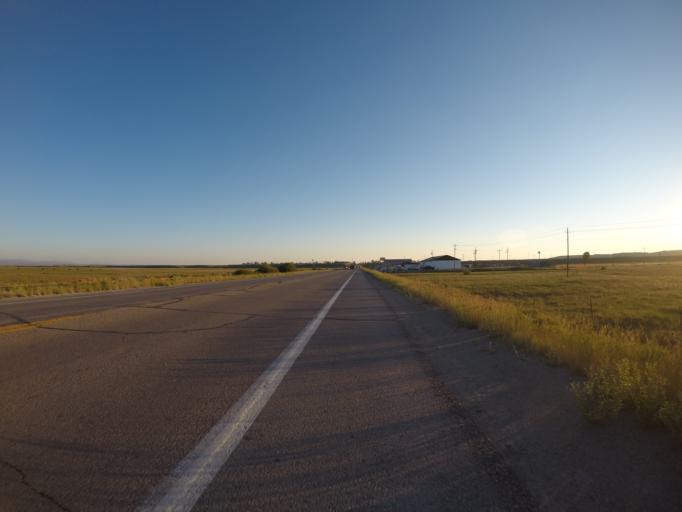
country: US
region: Wyoming
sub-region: Sublette County
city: Marbleton
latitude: 42.5422
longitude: -110.1096
